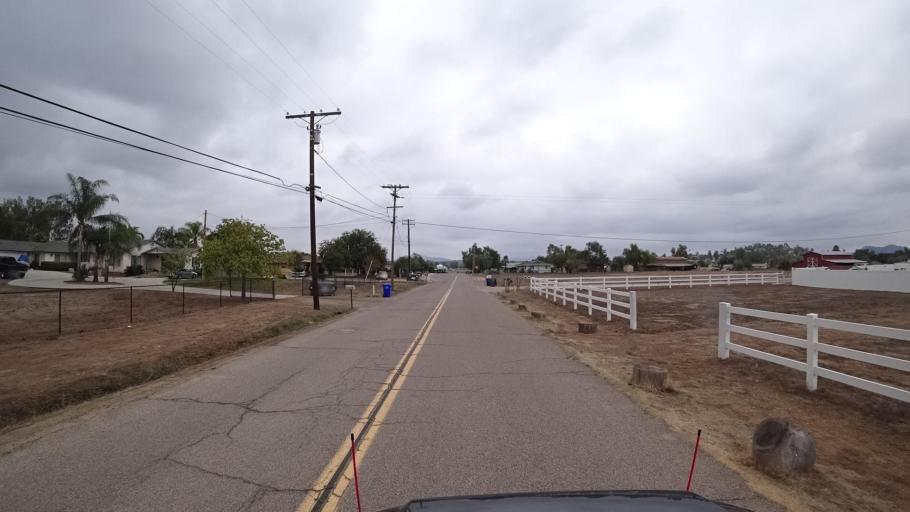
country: US
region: California
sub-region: San Diego County
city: Ramona
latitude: 33.0318
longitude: -116.8742
